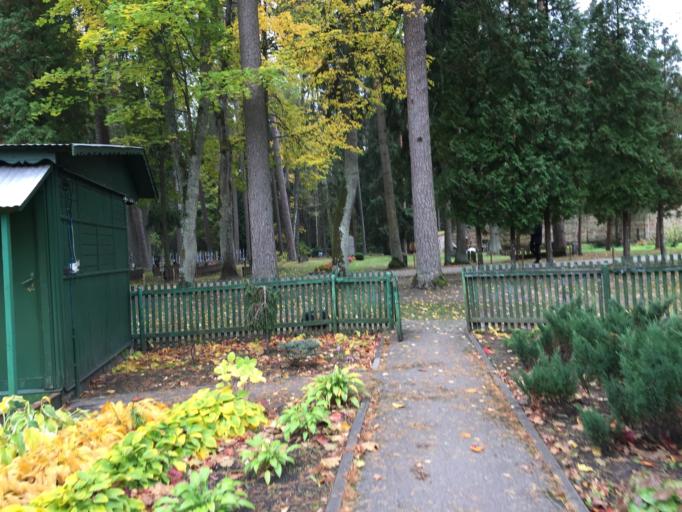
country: LV
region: Jelgava
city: Jelgava
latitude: 56.7336
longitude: 23.6927
